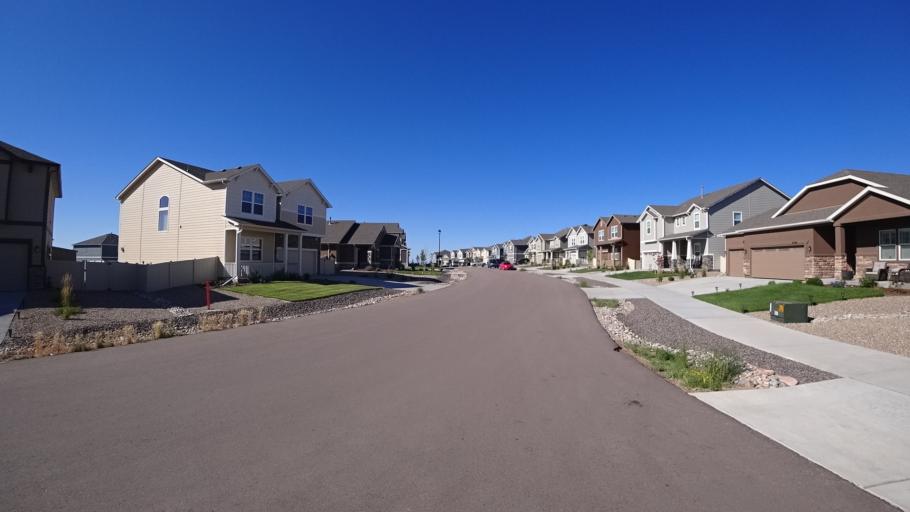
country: US
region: Colorado
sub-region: El Paso County
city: Cimarron Hills
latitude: 38.8957
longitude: -104.6767
